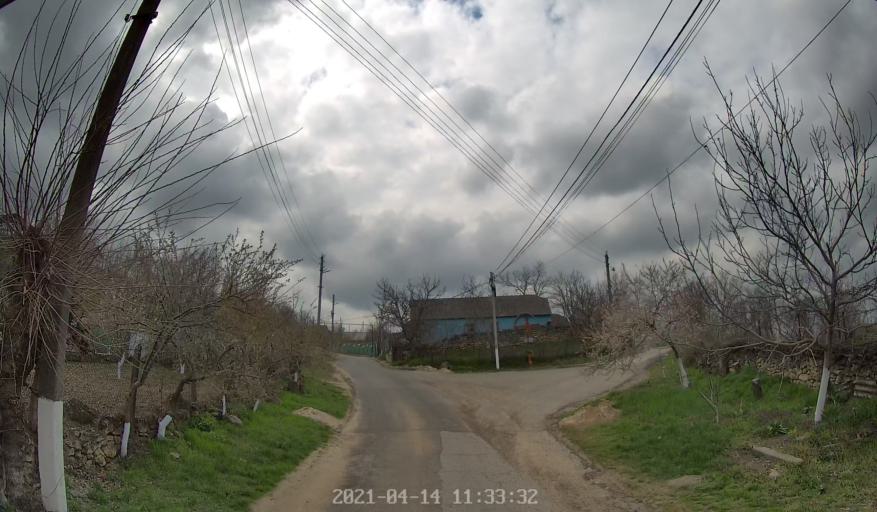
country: MD
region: Criuleni
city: Criuleni
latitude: 47.1795
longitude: 29.1651
